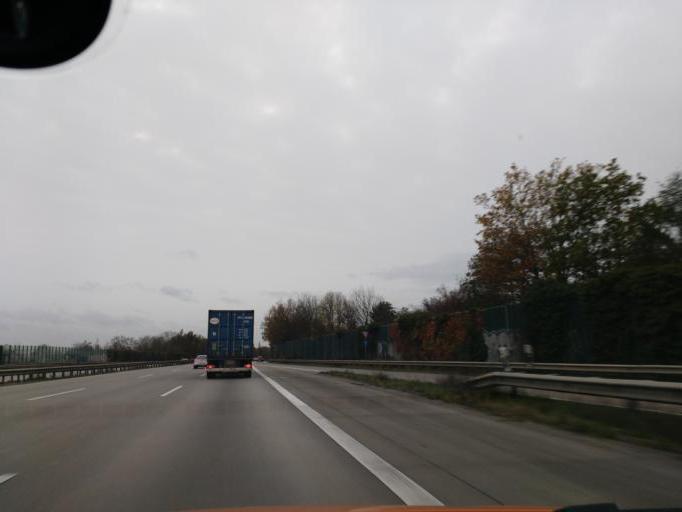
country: DE
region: Bremen
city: Bremen
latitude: 53.0272
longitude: 8.8542
